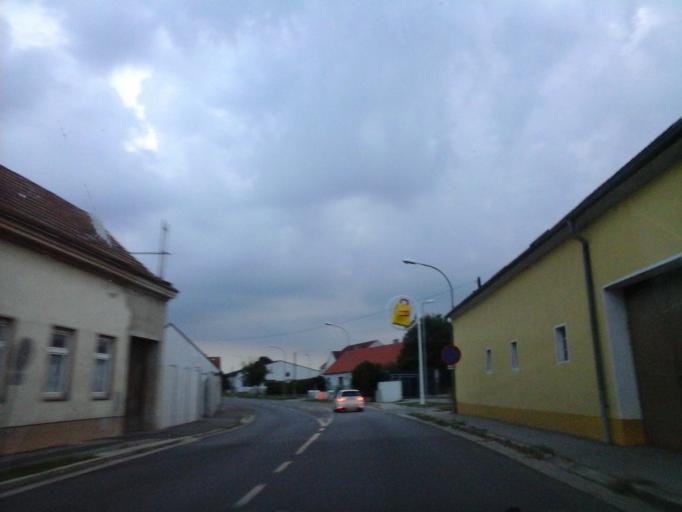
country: AT
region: Lower Austria
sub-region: Politischer Bezirk Ganserndorf
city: Durnkrut
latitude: 48.4717
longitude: 16.8526
